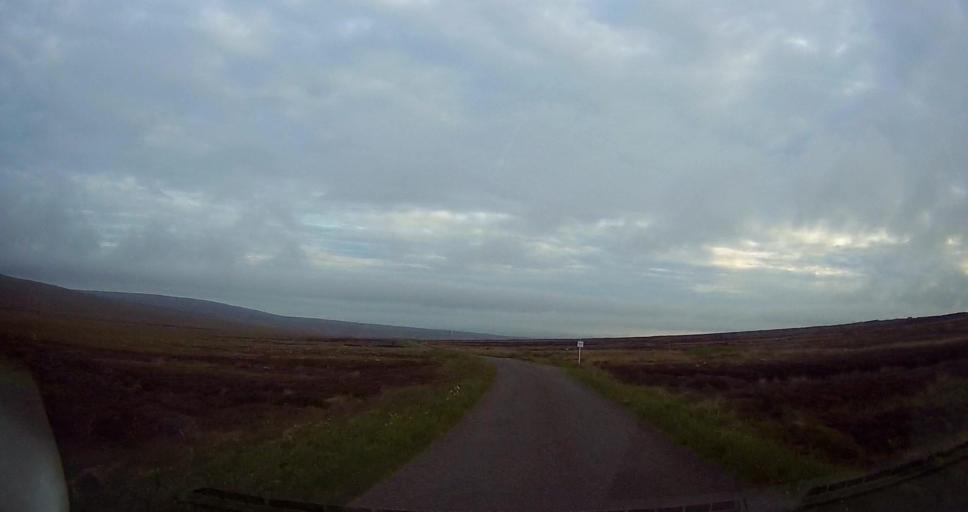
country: GB
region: Scotland
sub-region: Orkney Islands
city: Stromness
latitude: 59.1013
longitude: -3.1467
